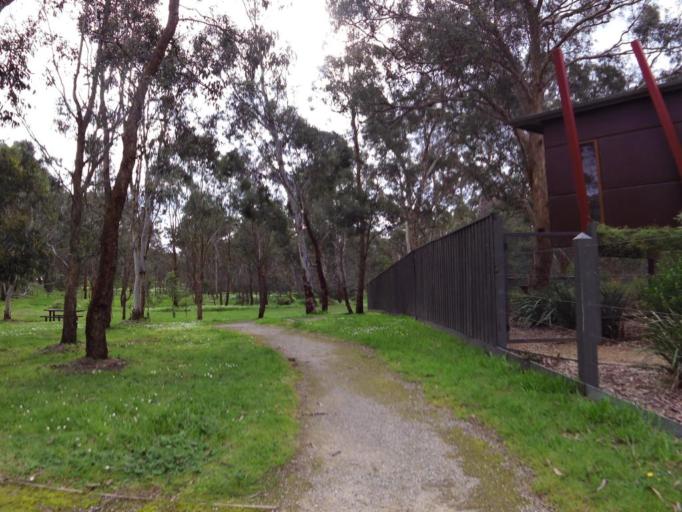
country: AU
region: Victoria
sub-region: Nillumbik
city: Eltham
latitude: -37.7461
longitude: 145.1720
